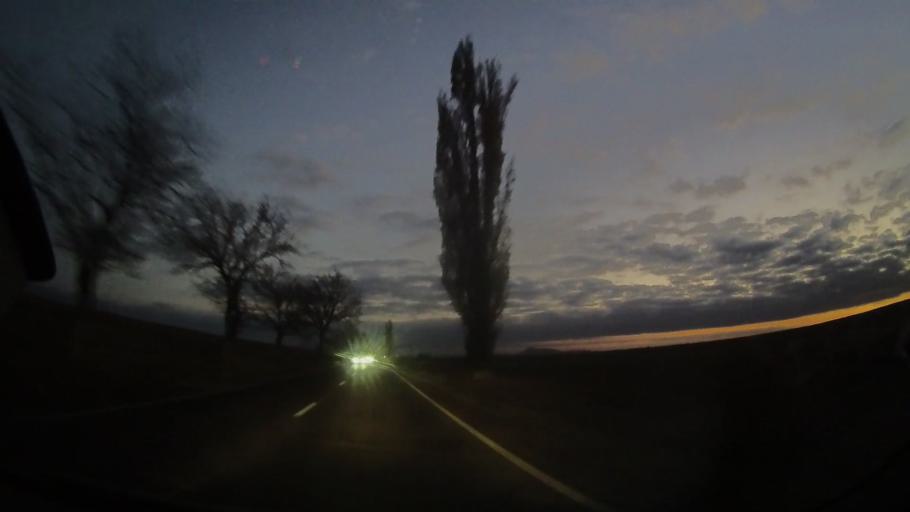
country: RO
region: Tulcea
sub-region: Comuna Frecatei
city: Cataloi
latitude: 45.0876
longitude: 28.7408
